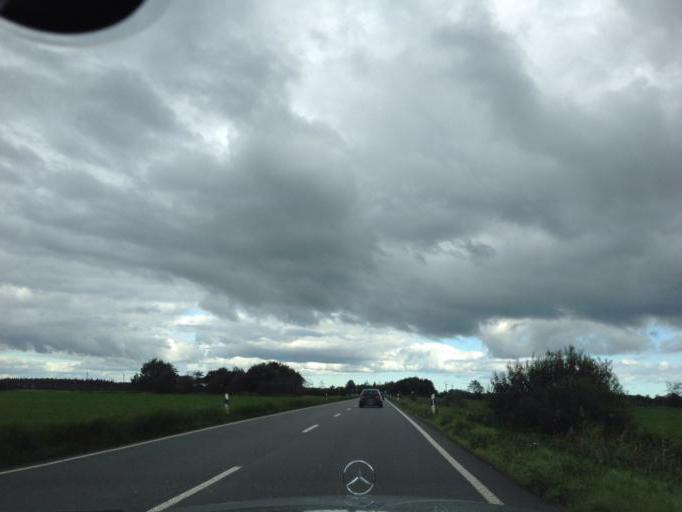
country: DE
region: Schleswig-Holstein
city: Stadum
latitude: 54.7432
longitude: 9.0671
